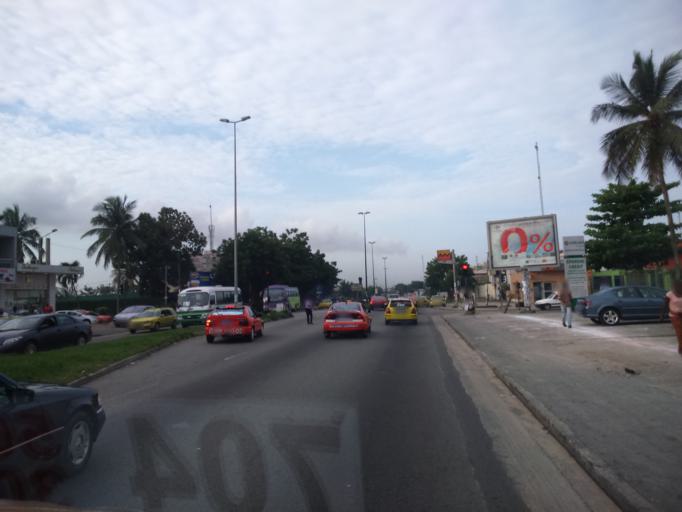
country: CI
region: Lagunes
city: Abobo
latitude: 5.3753
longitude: -3.9985
